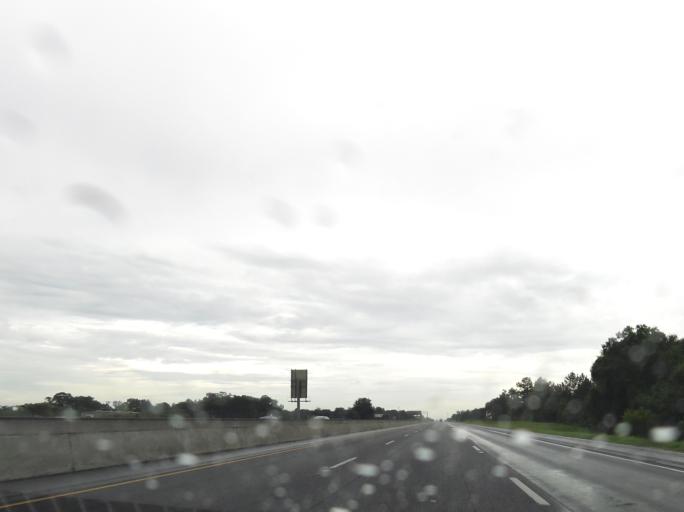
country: US
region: Georgia
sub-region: Lowndes County
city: Hahira
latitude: 30.9773
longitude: -83.3836
